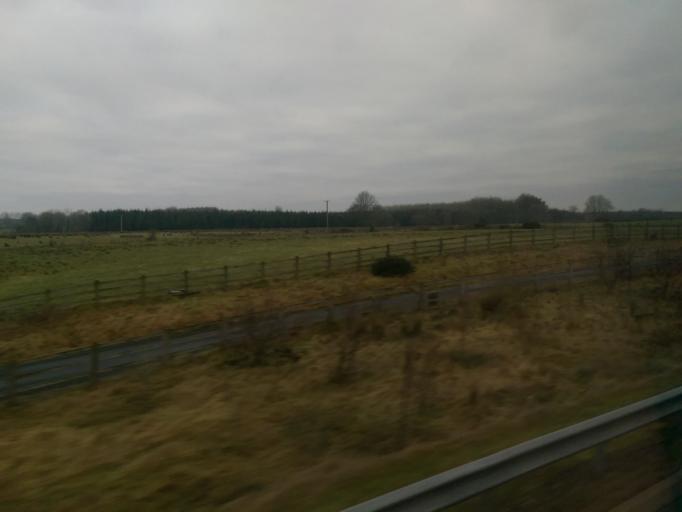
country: IE
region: Connaught
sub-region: County Galway
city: Loughrea
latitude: 53.2854
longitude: -8.4661
